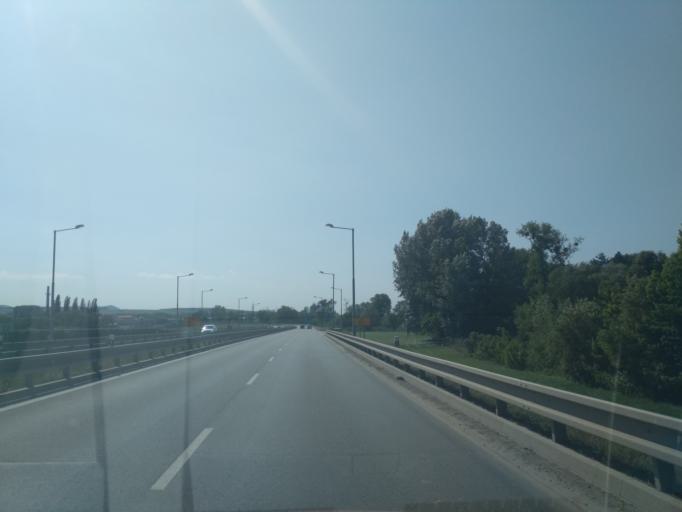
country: SK
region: Presovsky
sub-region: Okres Presov
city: Presov
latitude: 48.9733
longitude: 21.2453
